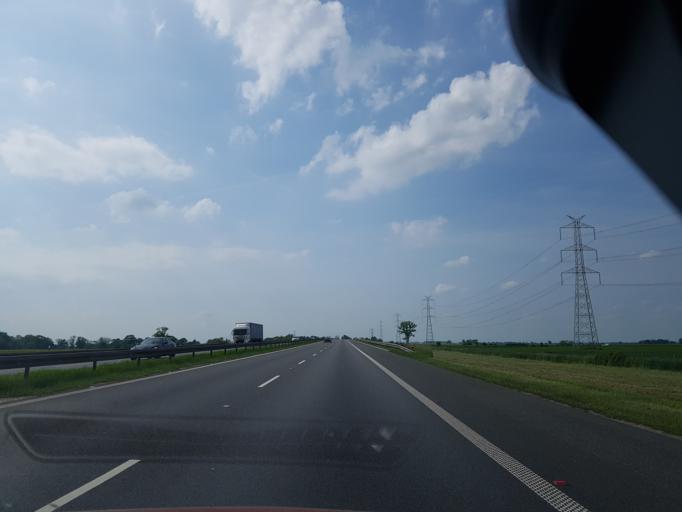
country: PL
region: Lower Silesian Voivodeship
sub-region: Powiat olawski
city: Wierzbno
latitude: 50.9302
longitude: 17.1201
